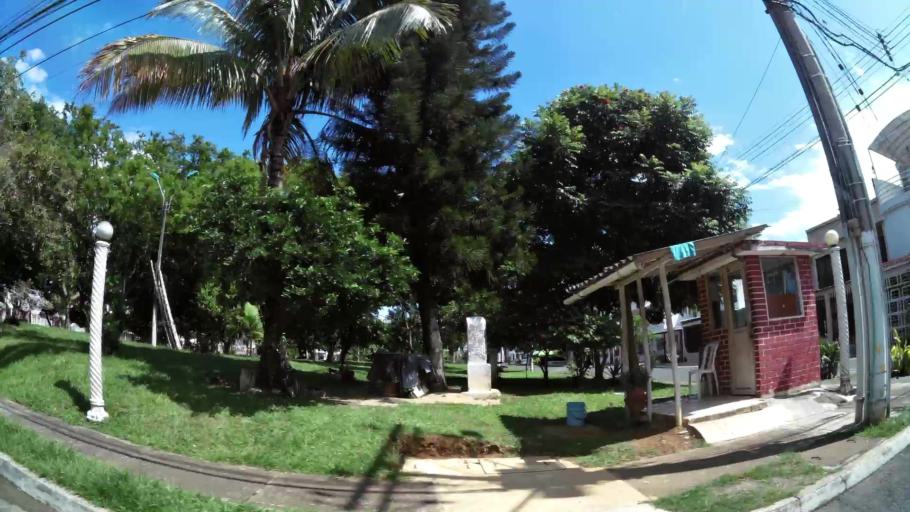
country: CO
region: Valle del Cauca
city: Cali
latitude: 3.3964
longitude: -76.5183
